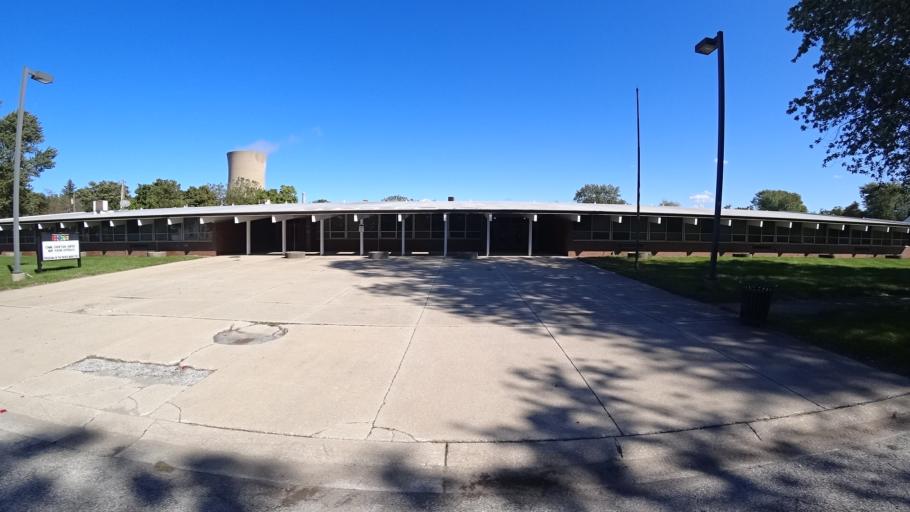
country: US
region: Indiana
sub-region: LaPorte County
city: Michigan City
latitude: 41.7114
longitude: -86.9158
